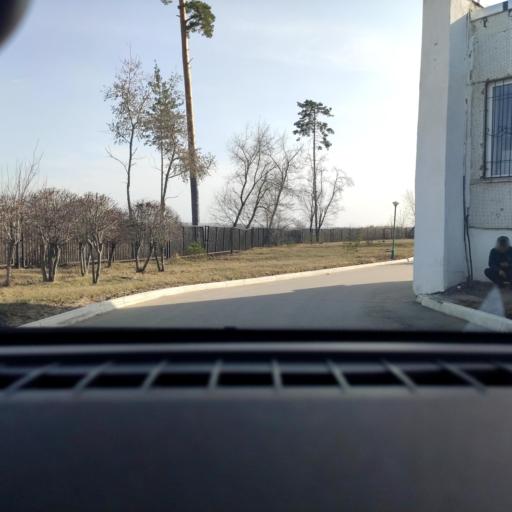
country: RU
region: Samara
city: Tol'yatti
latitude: 53.4986
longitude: 49.3600
